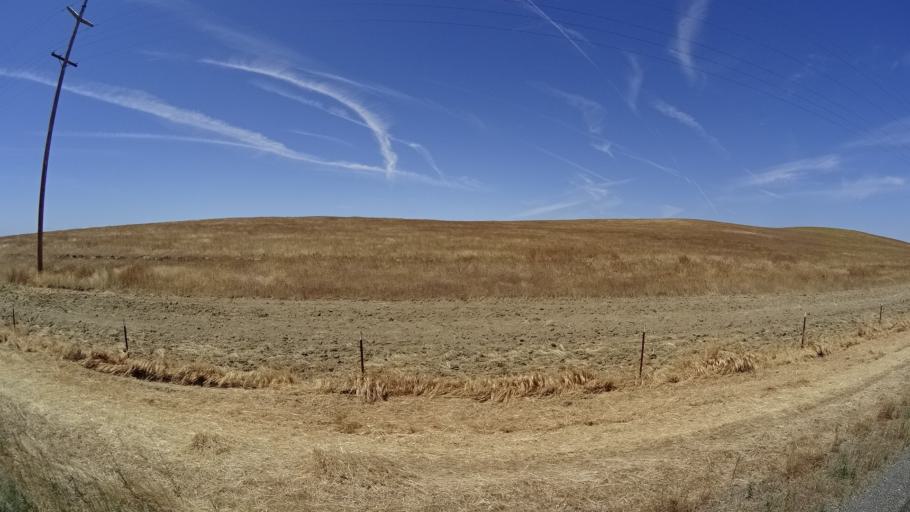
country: US
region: California
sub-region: Kings County
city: Kettleman City
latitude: 35.8634
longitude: -119.9153
